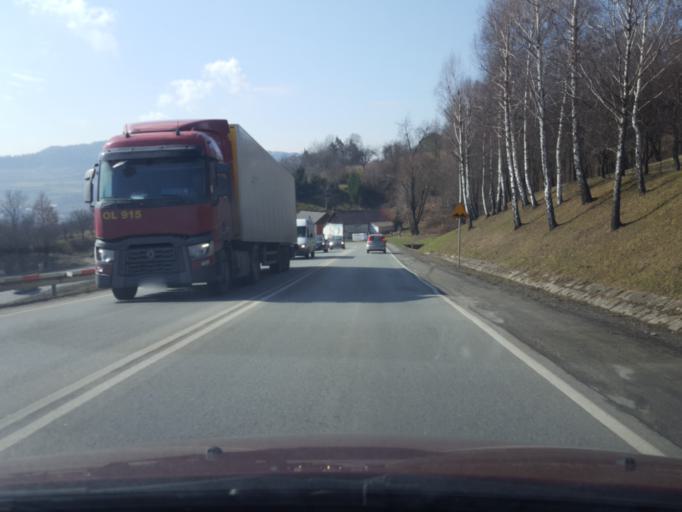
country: PL
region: Lesser Poland Voivodeship
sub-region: Powiat nowosadecki
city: Lososina Dolna
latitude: 49.7230
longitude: 20.6415
